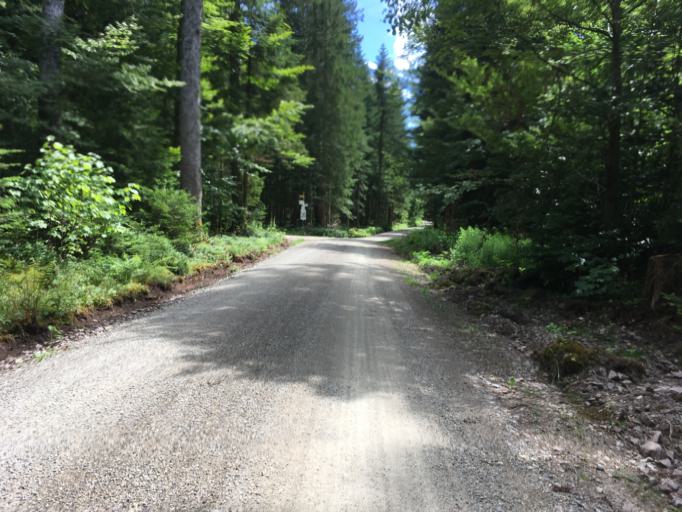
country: DE
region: Baden-Wuerttemberg
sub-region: Karlsruhe Region
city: Baiersbronn
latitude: 48.5352
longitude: 8.4253
